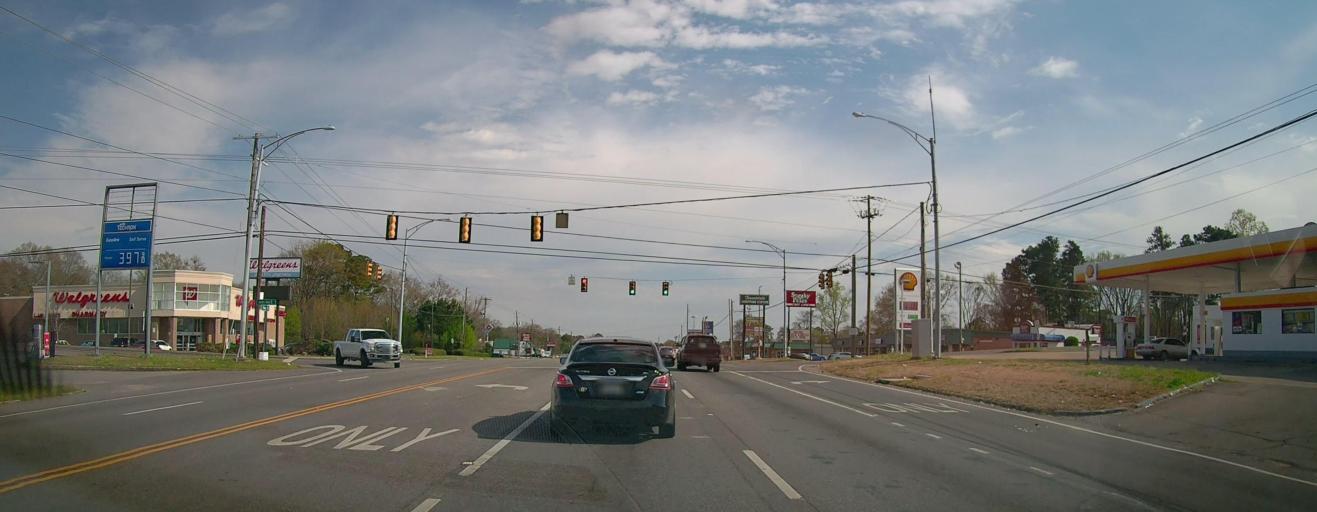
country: US
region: Alabama
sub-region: Jefferson County
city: Forestdale
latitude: 33.5685
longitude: -86.8986
